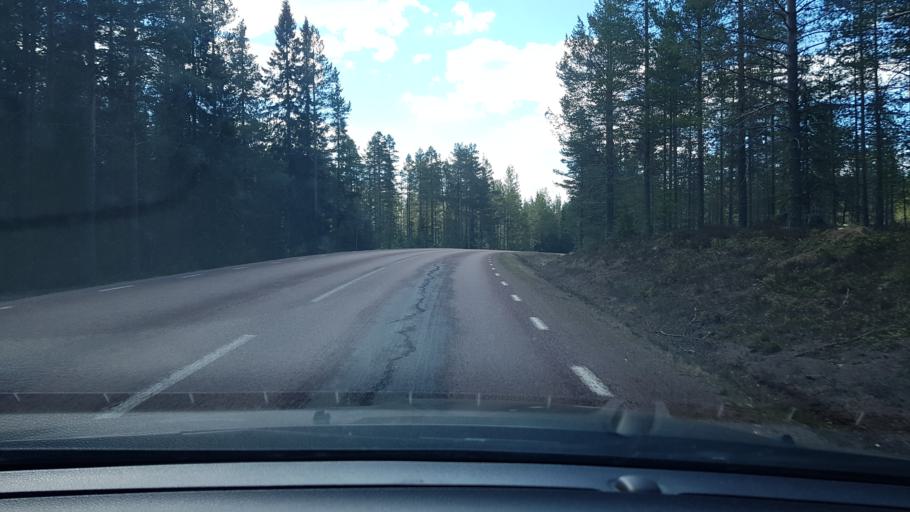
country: SE
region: Dalarna
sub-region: Malung-Saelens kommun
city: Malung
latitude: 61.0592
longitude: 13.4581
